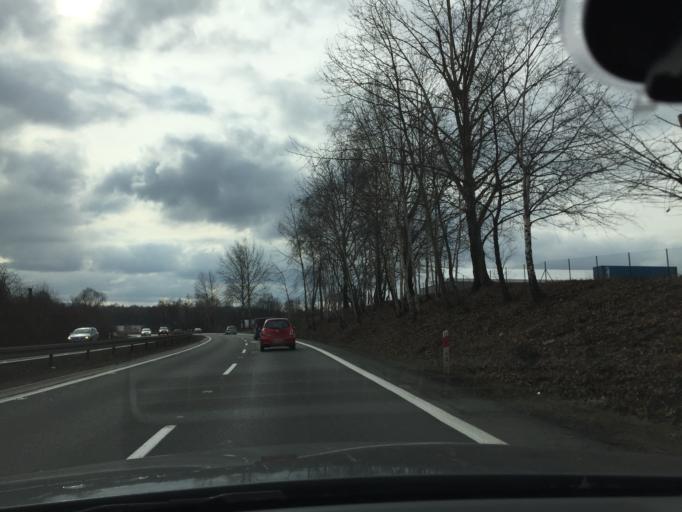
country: PL
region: Silesian Voivodeship
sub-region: Powiat bielski
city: Mazancowice
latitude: 49.8809
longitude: 18.9981
